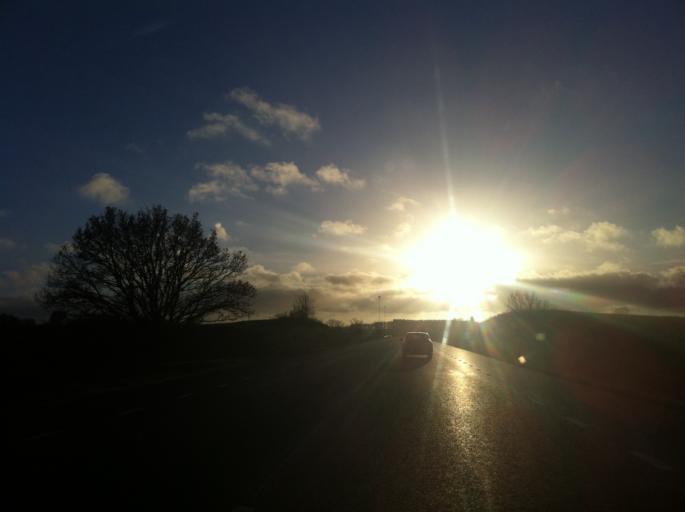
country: SE
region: Skane
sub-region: Hassleholms Kommun
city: Tormestorp
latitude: 56.0730
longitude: 13.7439
